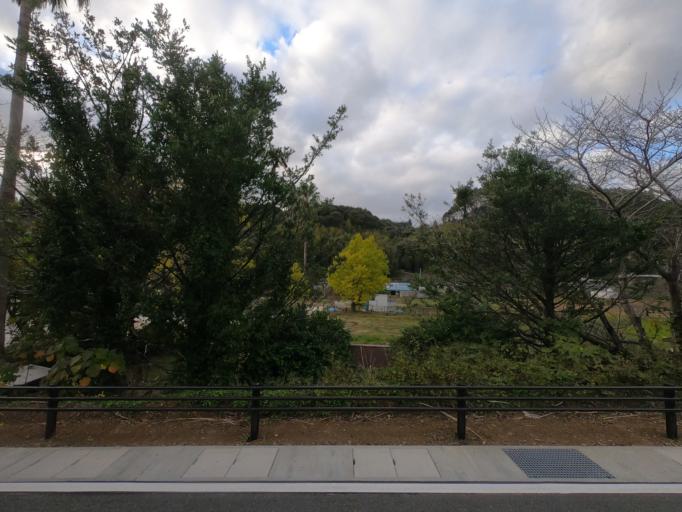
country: JP
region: Kumamoto
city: Minamata
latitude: 32.2423
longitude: 130.4680
